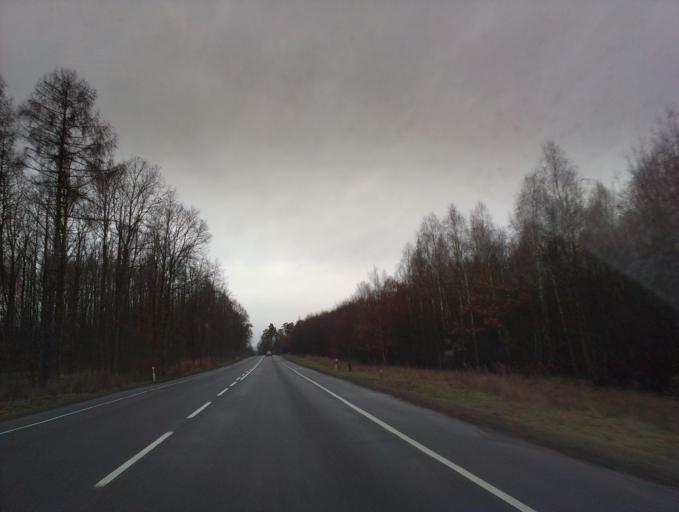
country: PL
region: Greater Poland Voivodeship
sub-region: Powiat chodzieski
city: Budzyn
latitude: 52.9310
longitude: 16.9657
